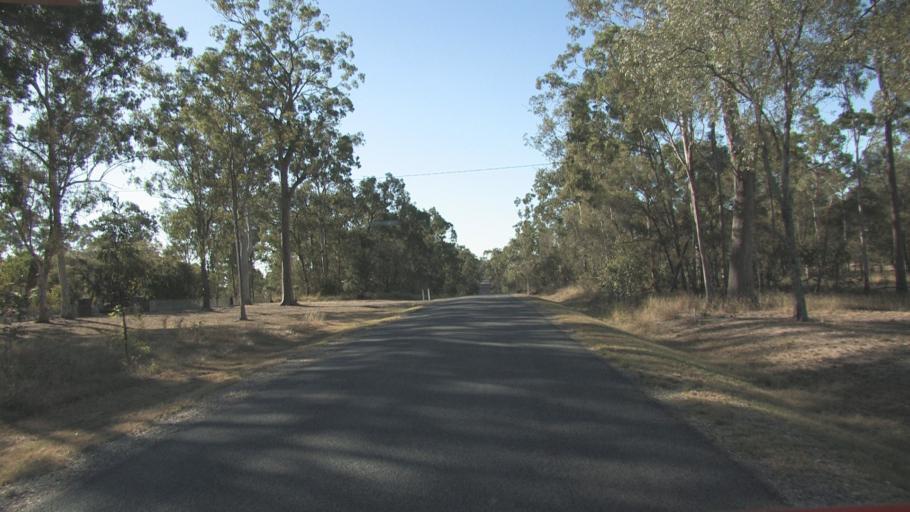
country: AU
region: Queensland
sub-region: Logan
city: North Maclean
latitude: -27.7983
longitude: 153.0258
